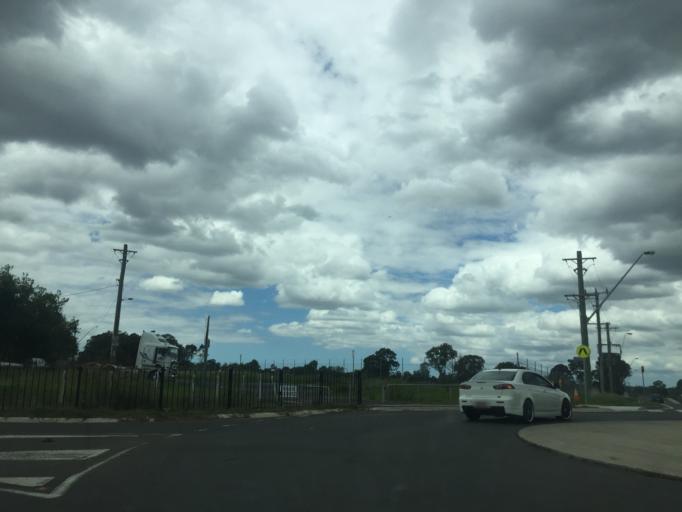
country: AU
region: New South Wales
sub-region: Blacktown
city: Riverstone
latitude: -33.7045
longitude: 150.8744
